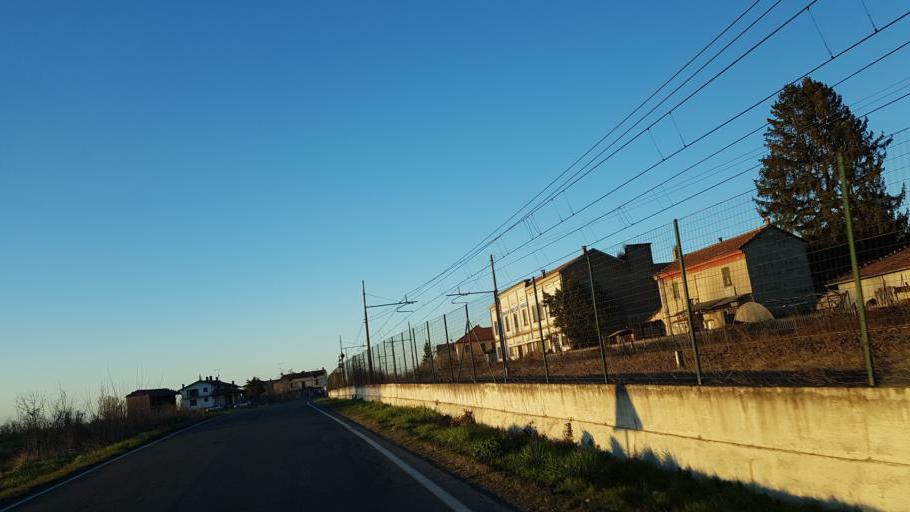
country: IT
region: Piedmont
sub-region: Provincia di Alessandria
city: Villalvernia
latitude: 44.8123
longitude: 8.8545
